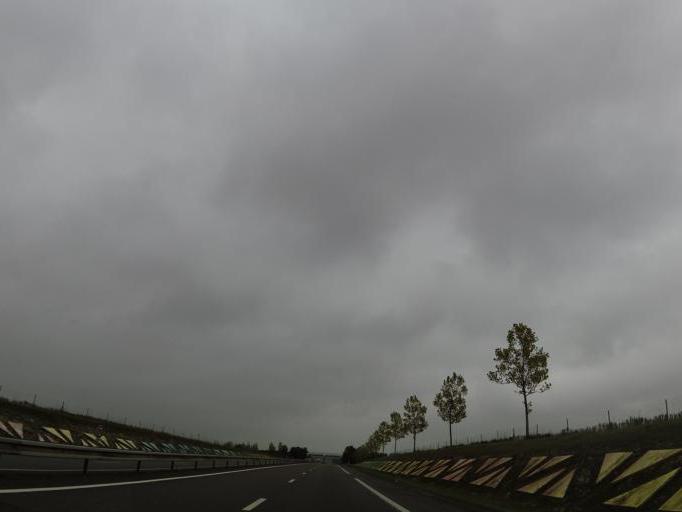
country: FR
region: Champagne-Ardenne
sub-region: Departement de la Marne
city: Courtisols
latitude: 49.0289
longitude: 4.4926
